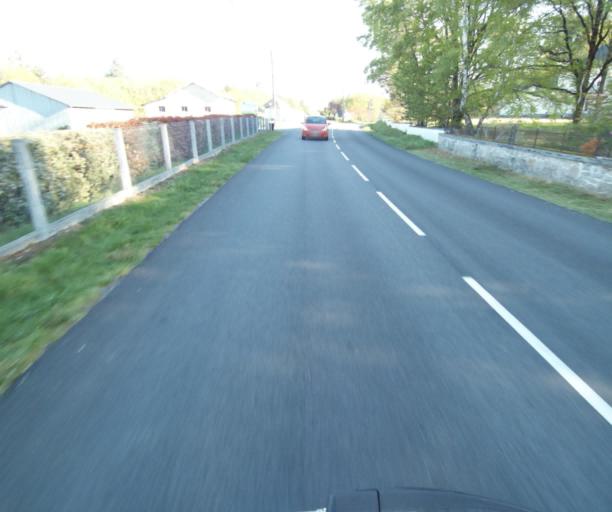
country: FR
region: Limousin
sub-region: Departement de la Correze
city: Correze
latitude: 45.3415
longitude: 1.8743
